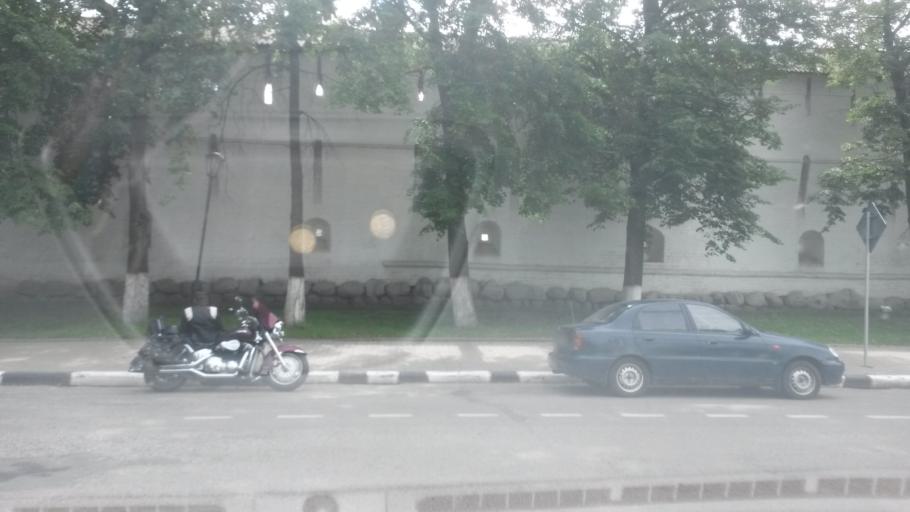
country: RU
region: Jaroslavl
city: Yaroslavl
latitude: 57.6222
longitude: 39.8912
